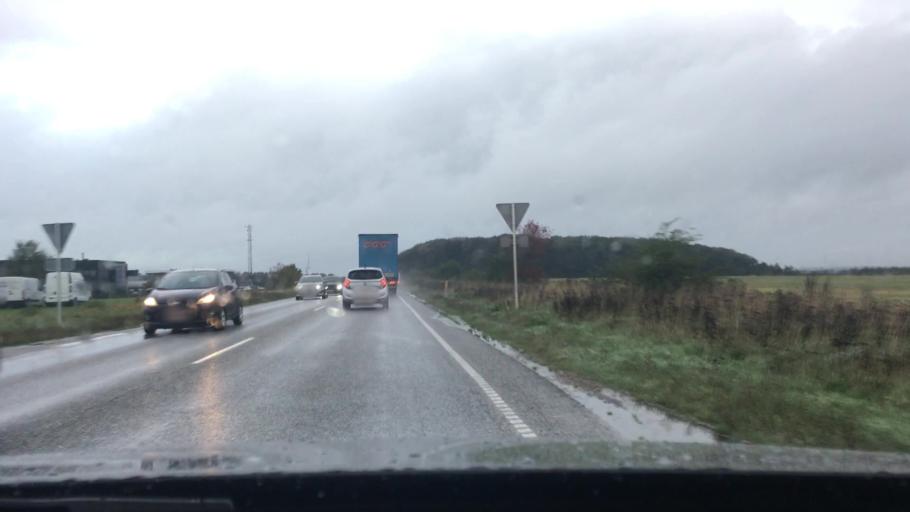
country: DK
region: Central Jutland
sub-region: Holstebro Kommune
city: Holstebro
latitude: 56.3366
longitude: 8.6461
